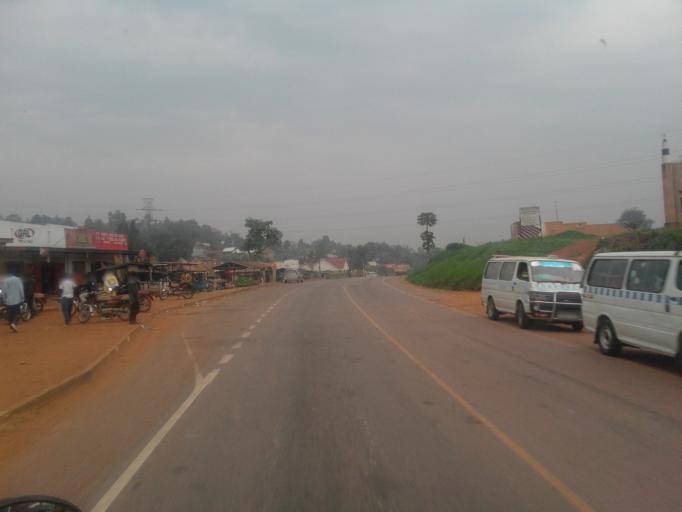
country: UG
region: Central Region
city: Lugazi
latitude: 0.3848
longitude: 32.8639
